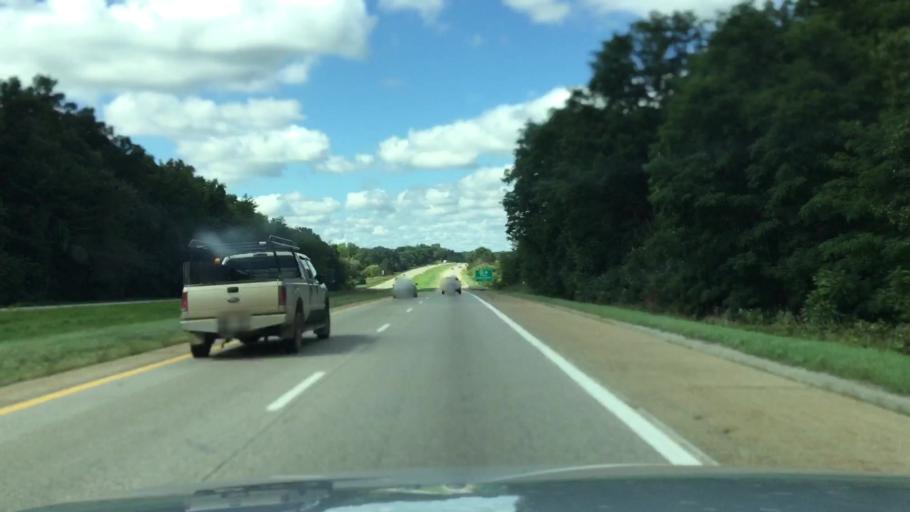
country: US
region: Michigan
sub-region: Calhoun County
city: Albion
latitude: 42.2623
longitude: -84.6863
